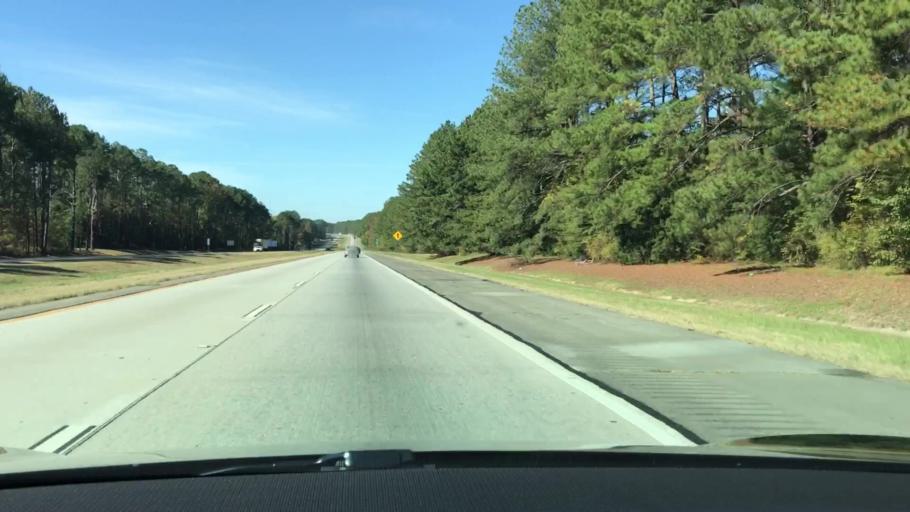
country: US
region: Georgia
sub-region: Taliaferro County
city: Crawfordville
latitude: 33.5300
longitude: -82.9116
